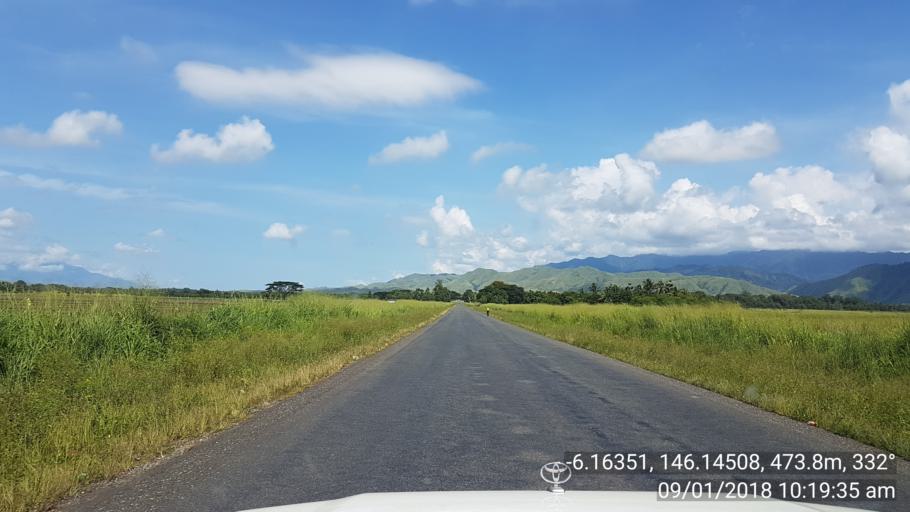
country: PG
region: Eastern Highlands
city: Kainantu
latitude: -6.1639
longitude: 146.1448
